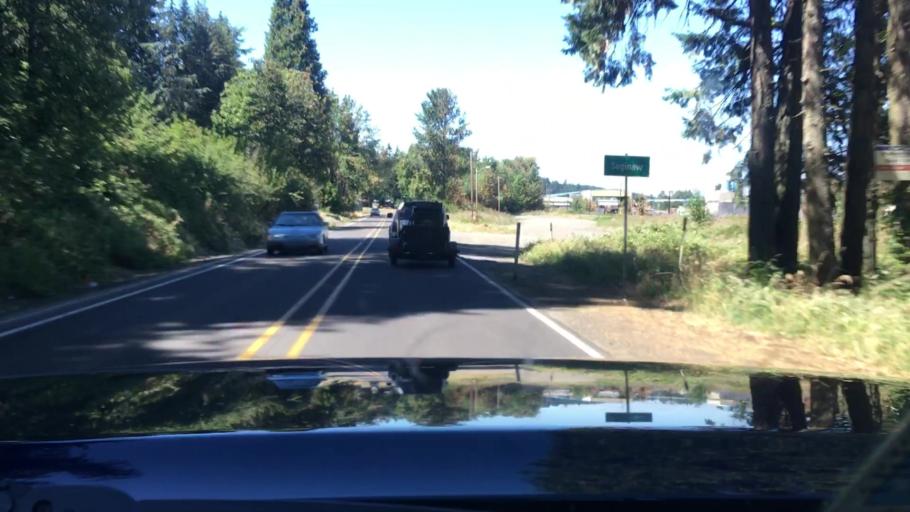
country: US
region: Oregon
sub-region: Lane County
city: Cottage Grove
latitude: 43.8281
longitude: -123.0445
